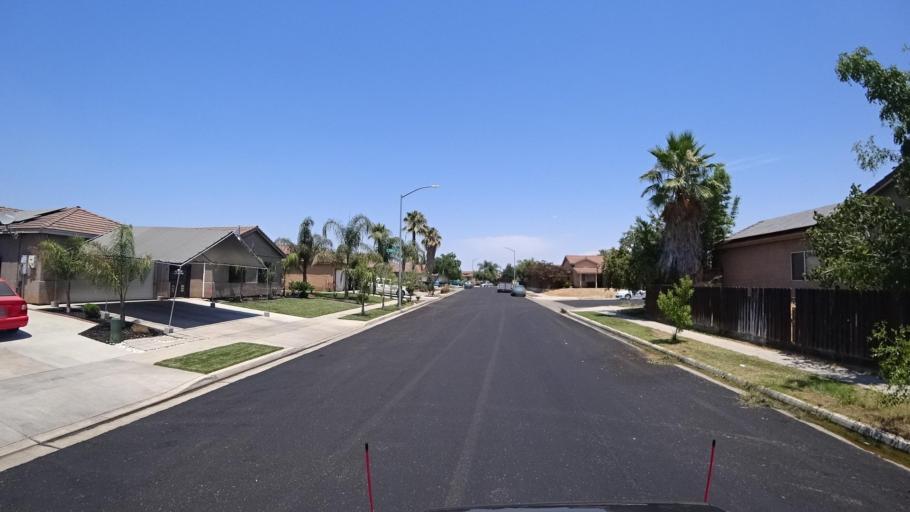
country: US
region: California
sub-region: Fresno County
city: Sunnyside
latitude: 36.7423
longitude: -119.6771
